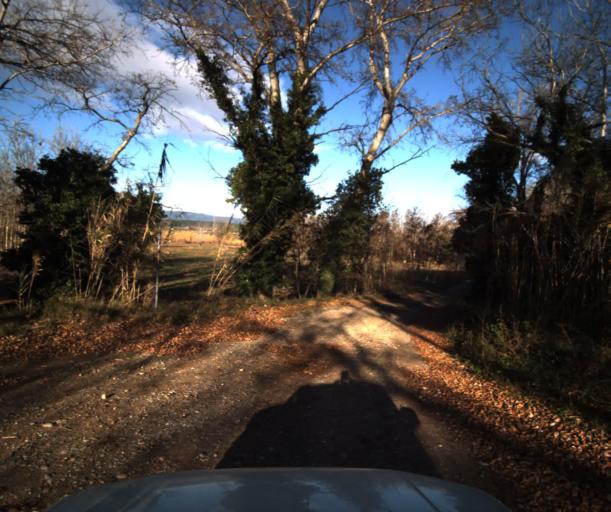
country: FR
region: Provence-Alpes-Cote d'Azur
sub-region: Departement du Vaucluse
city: Pertuis
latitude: 43.6750
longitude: 5.4779
